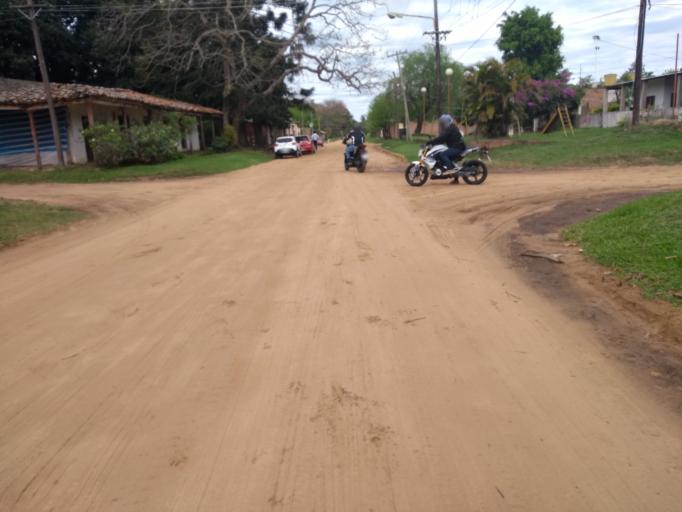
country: AR
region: Corrientes
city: San Luis del Palmar
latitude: -27.4565
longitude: -58.6584
